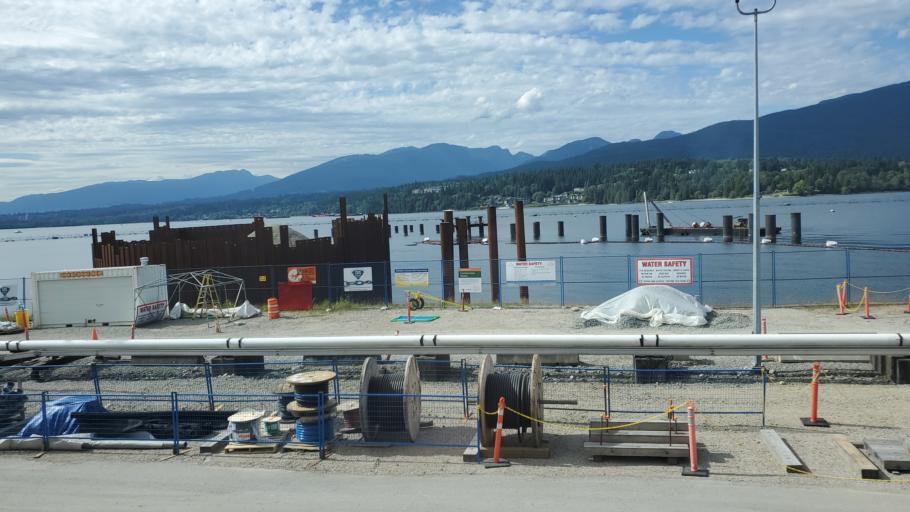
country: CA
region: British Columbia
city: Burnaby
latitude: 49.2897
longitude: -122.9528
